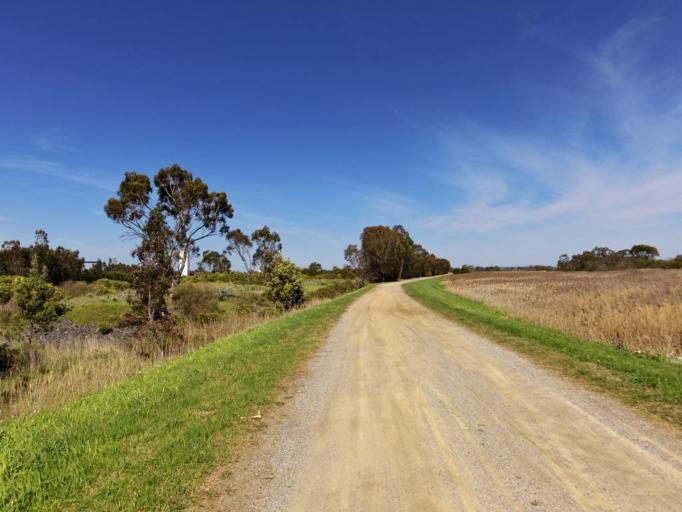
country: AU
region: Victoria
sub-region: Greater Dandenong
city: Keysborough
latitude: -38.0230
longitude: 145.1875
